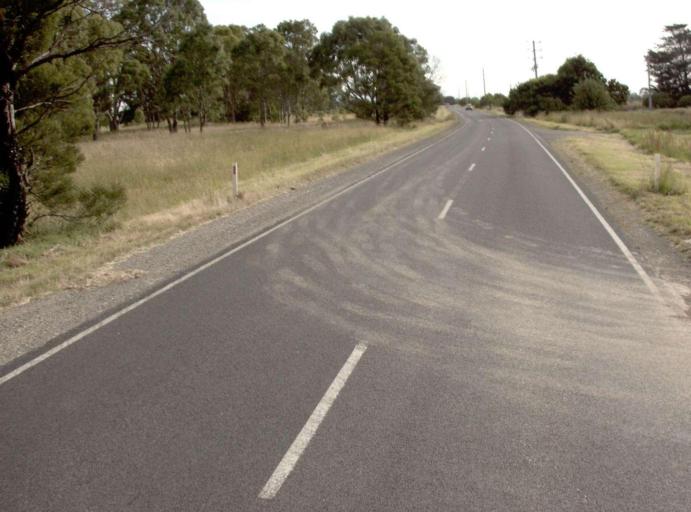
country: AU
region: Victoria
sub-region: Latrobe
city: Traralgon
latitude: -38.0966
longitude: 146.5972
